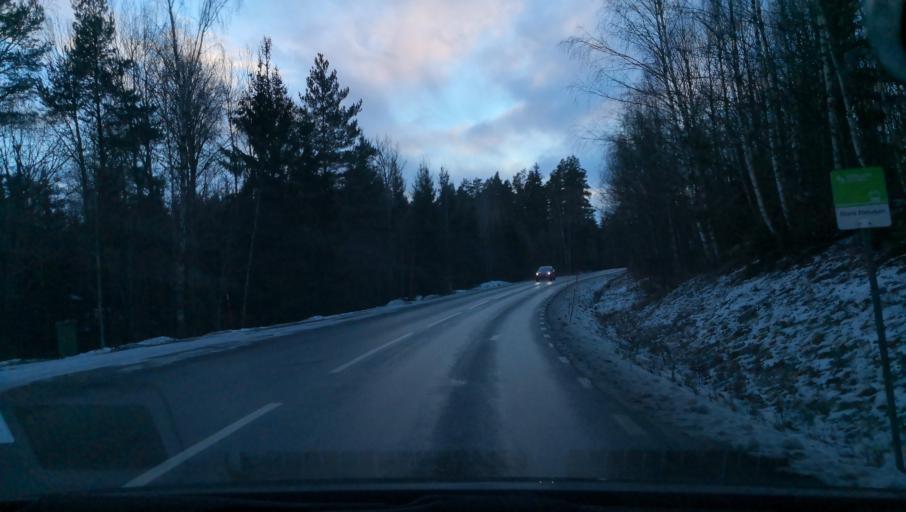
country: SE
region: Soedermanland
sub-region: Flens Kommun
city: Halleforsnas
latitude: 59.2154
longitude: 16.2805
